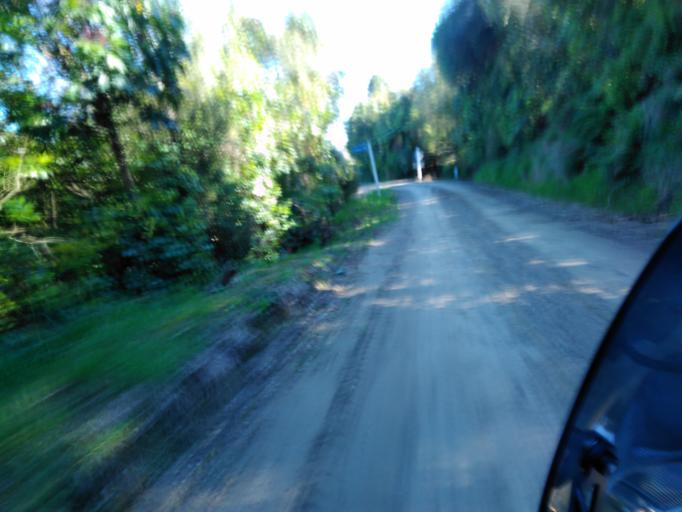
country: NZ
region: Gisborne
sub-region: Gisborne District
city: Gisborne
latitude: -38.3871
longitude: 177.6227
